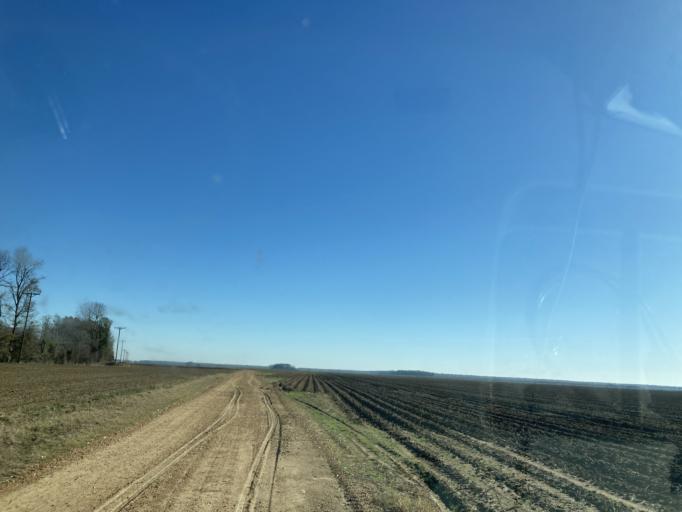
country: US
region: Mississippi
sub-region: Sharkey County
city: Rolling Fork
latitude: 32.8699
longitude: -90.6921
